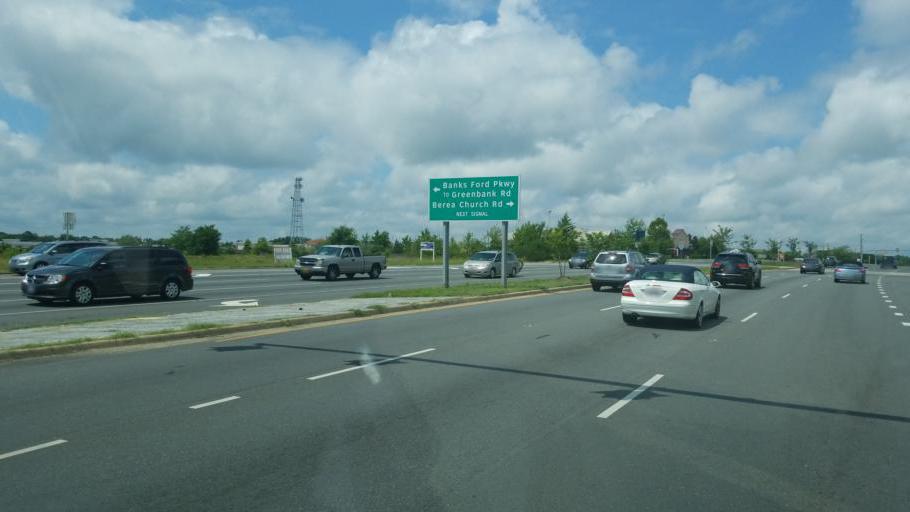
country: US
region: Virginia
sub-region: Stafford County
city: Falmouth
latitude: 38.3590
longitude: -77.5178
